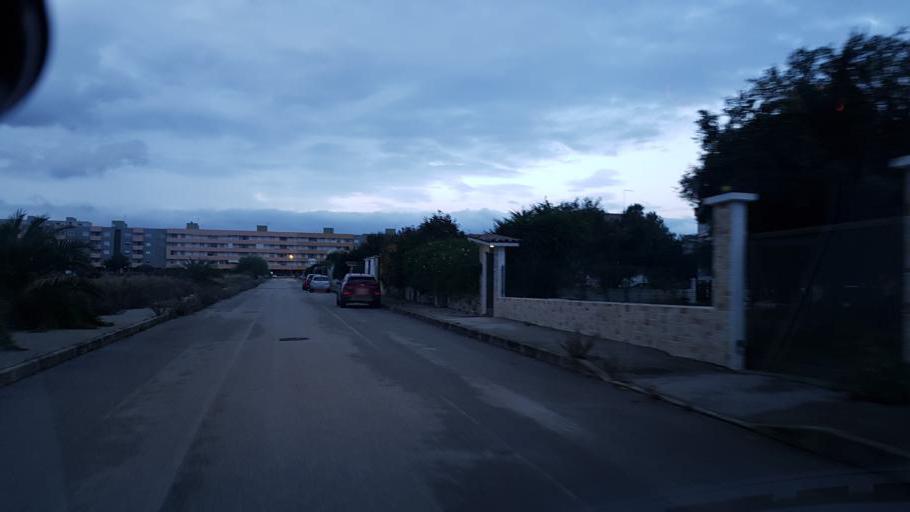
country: IT
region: Apulia
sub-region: Provincia di Taranto
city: Paolo VI
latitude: 40.5290
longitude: 17.2848
